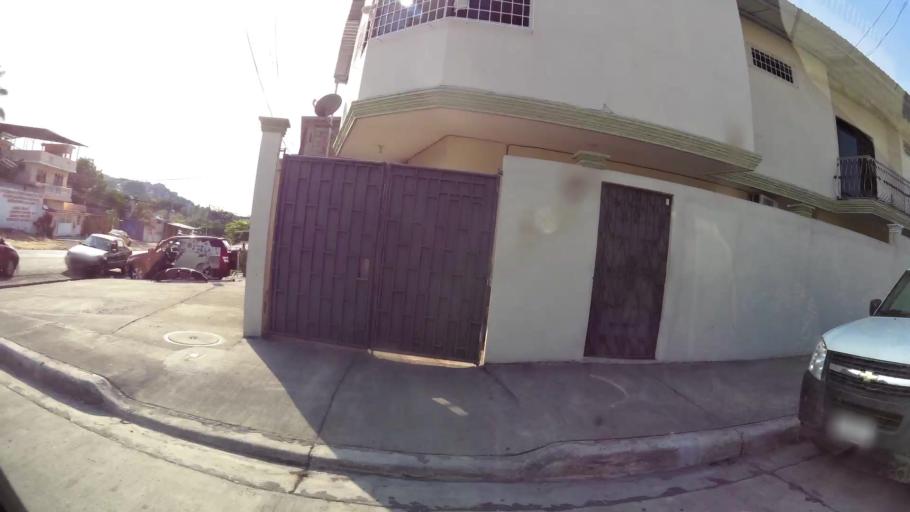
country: EC
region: Guayas
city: Guayaquil
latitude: -2.1549
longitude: -79.9093
